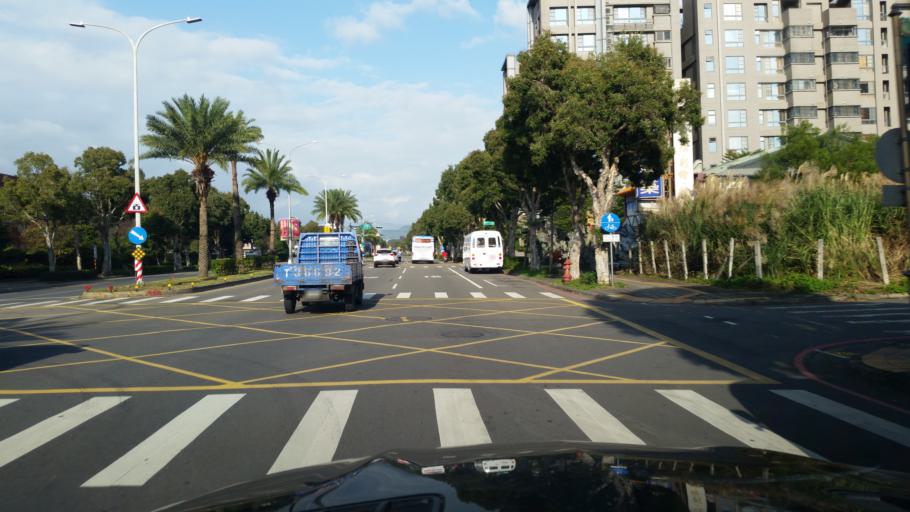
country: TW
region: Taiwan
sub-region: Taoyuan
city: Taoyuan
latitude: 25.0771
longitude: 121.3654
